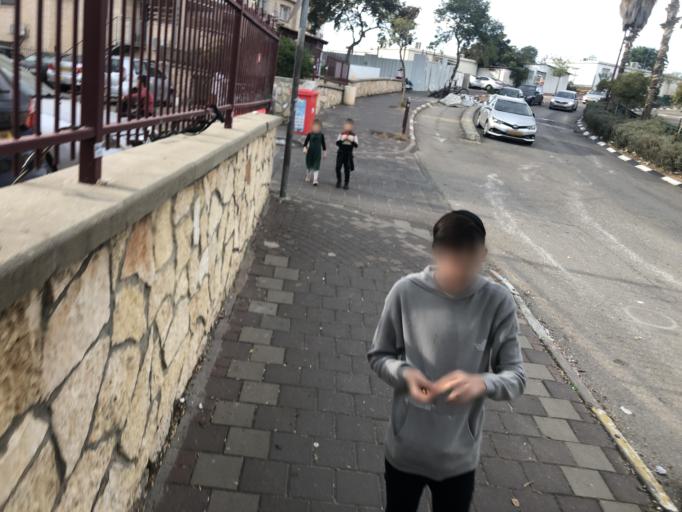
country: IL
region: Jerusalem
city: Modiin Ilit
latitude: 31.9377
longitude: 35.0366
